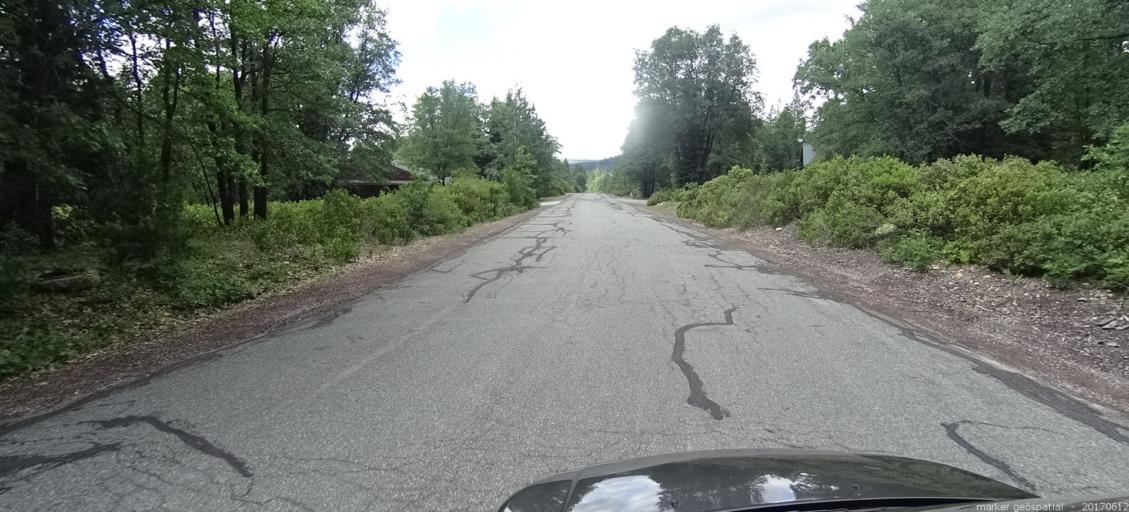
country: US
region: California
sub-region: Siskiyou County
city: Mount Shasta
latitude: 41.3123
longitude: -122.2832
